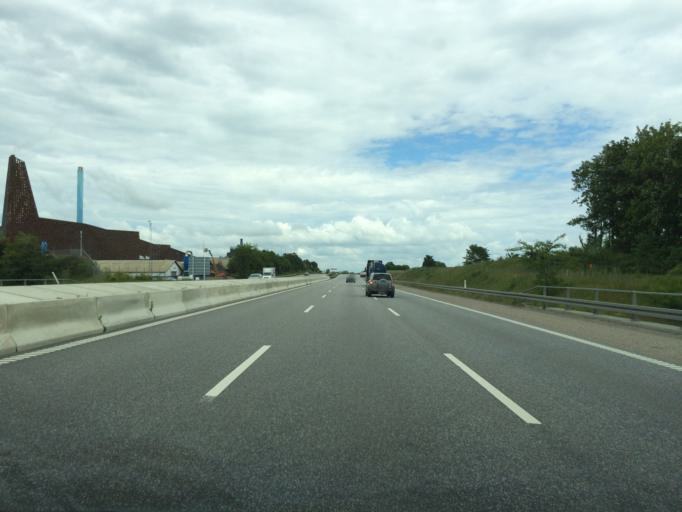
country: DK
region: Zealand
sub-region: Roskilde Kommune
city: Vindinge
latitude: 55.6354
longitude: 12.1178
